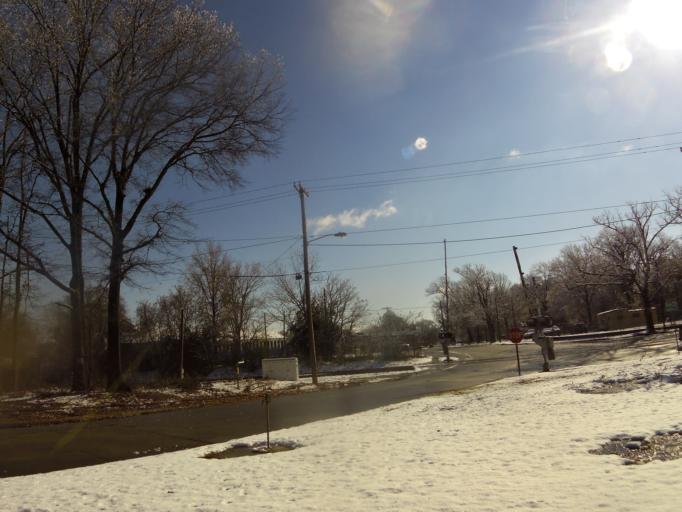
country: US
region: North Carolina
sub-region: Wilson County
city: Wilson
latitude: 35.7280
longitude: -77.9055
